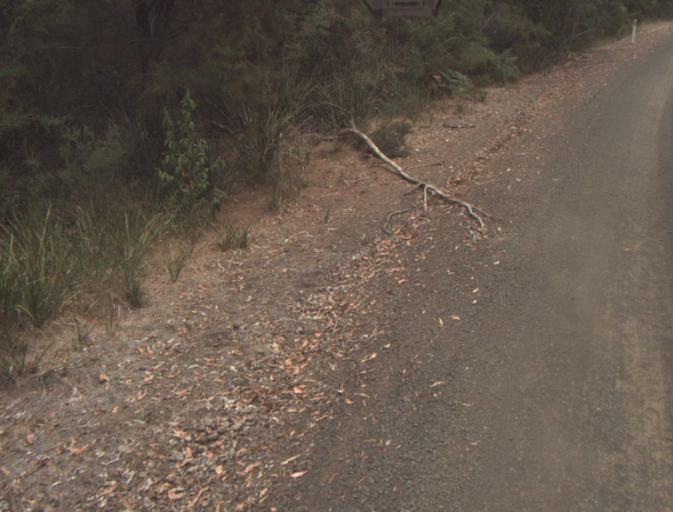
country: AU
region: Tasmania
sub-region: Launceston
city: Mayfield
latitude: -41.2740
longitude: 147.0513
